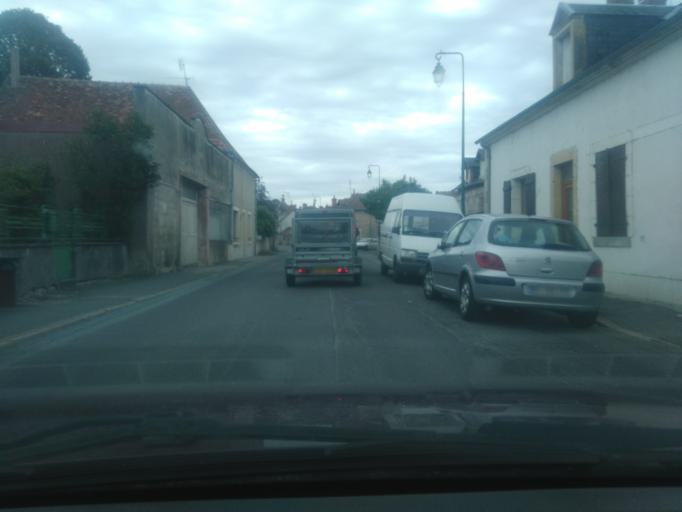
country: FR
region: Centre
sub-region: Departement du Cher
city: Charenton-du-Cher
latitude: 46.7304
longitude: 2.6401
